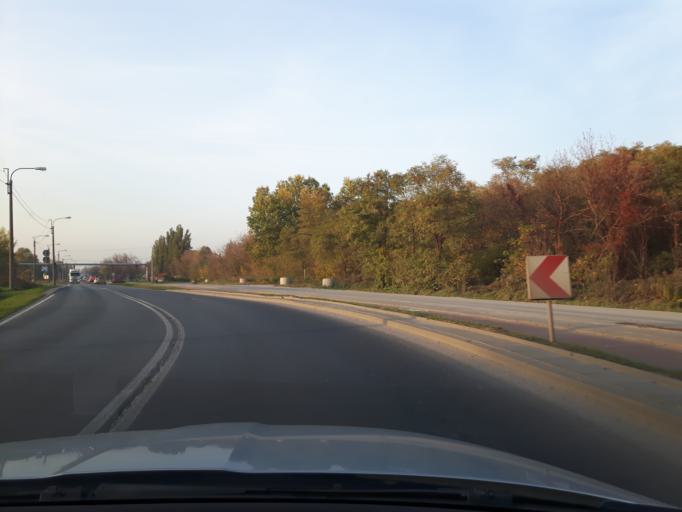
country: PL
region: Masovian Voivodeship
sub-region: Warszawa
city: Praga Poludnie
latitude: 52.2625
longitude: 21.0788
